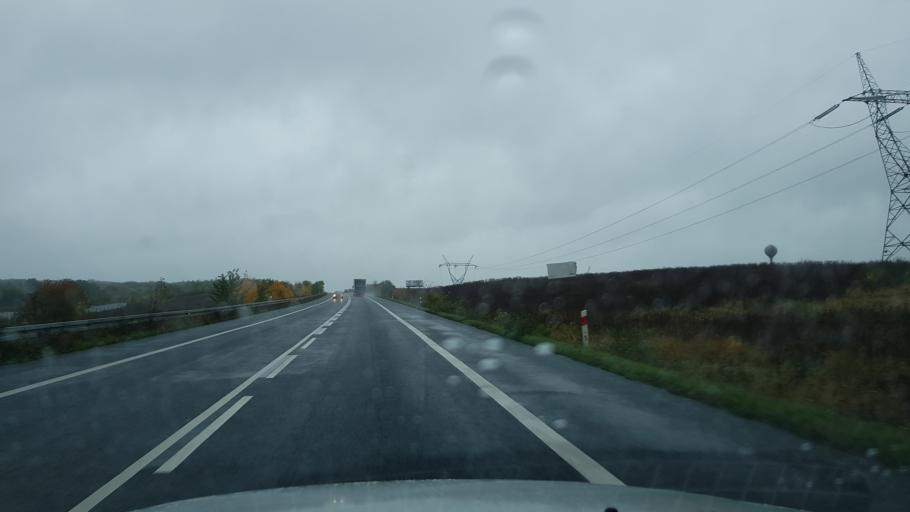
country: PL
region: West Pomeranian Voivodeship
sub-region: Powiat gryfinski
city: Stare Czarnowo
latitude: 53.2875
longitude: 14.7883
